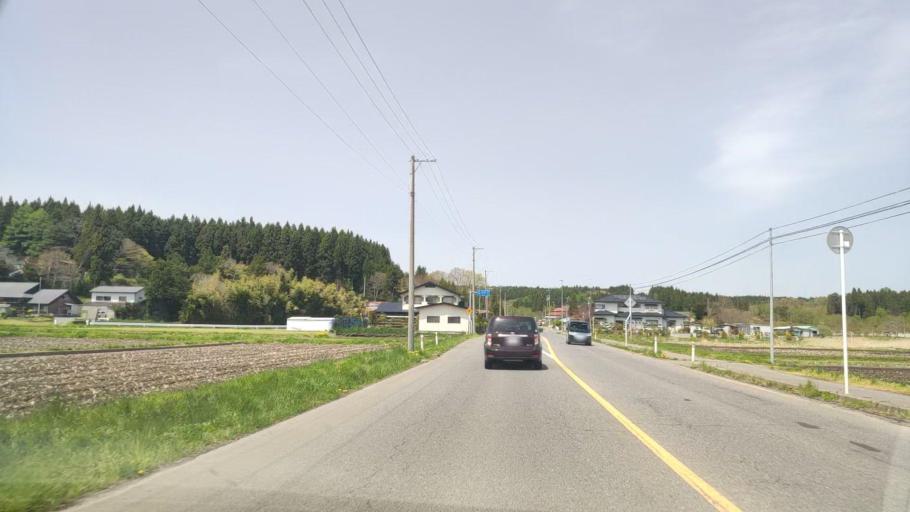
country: JP
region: Aomori
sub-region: Misawa Shi
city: Inuotose
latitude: 40.5597
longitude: 141.3855
